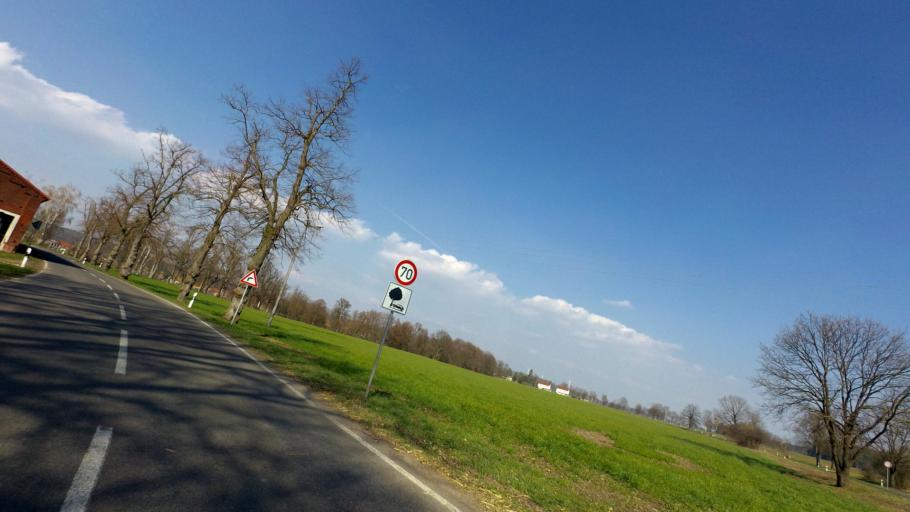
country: DE
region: Brandenburg
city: Dahme
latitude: 51.8979
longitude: 13.4854
